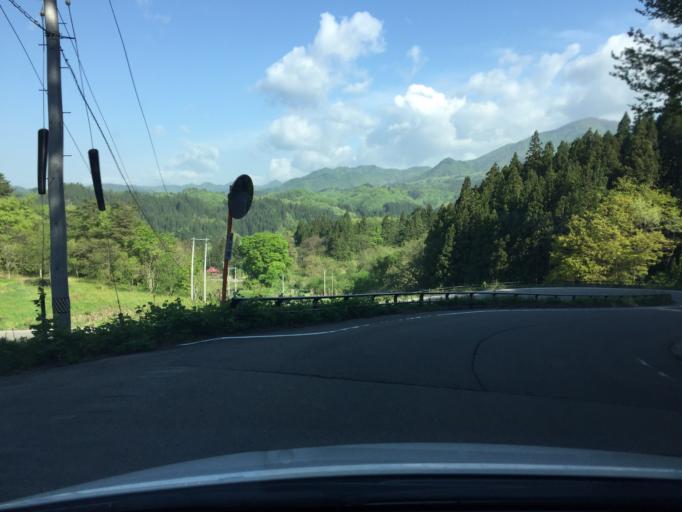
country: JP
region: Fukushima
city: Kitakata
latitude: 37.6851
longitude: 139.6762
